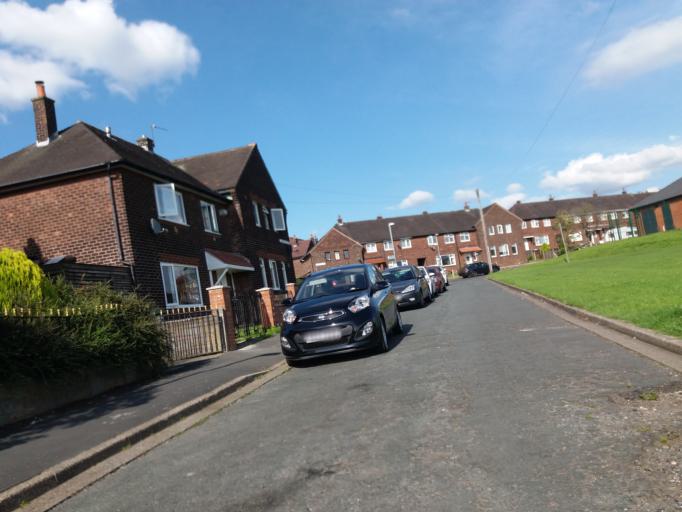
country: GB
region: England
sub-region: Lancashire
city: Coppull
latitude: 53.6433
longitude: -2.6449
